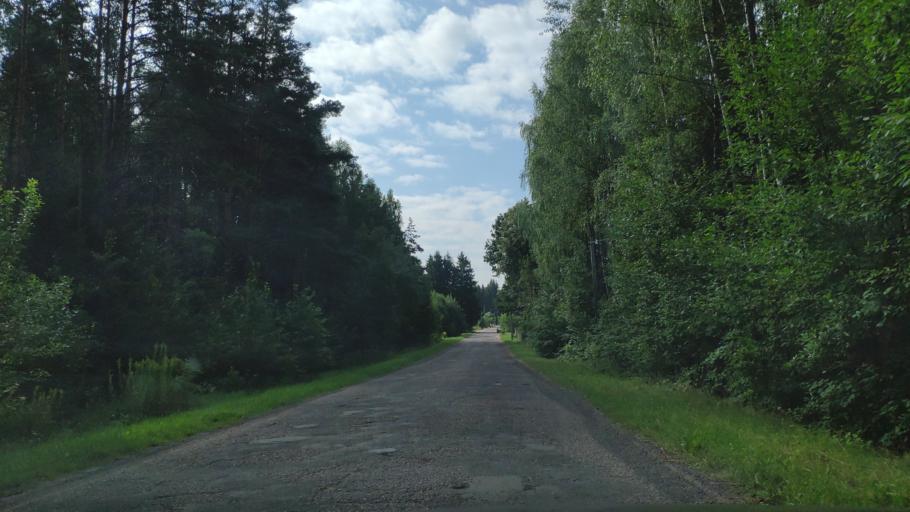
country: BY
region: Minsk
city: Zaslawye
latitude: 53.9798
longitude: 27.2896
